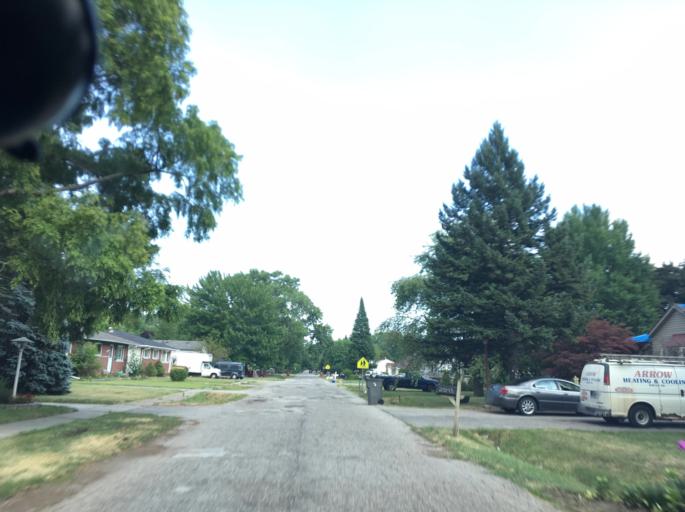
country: US
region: Michigan
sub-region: Macomb County
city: Fraser
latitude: 42.5460
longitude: -82.9153
